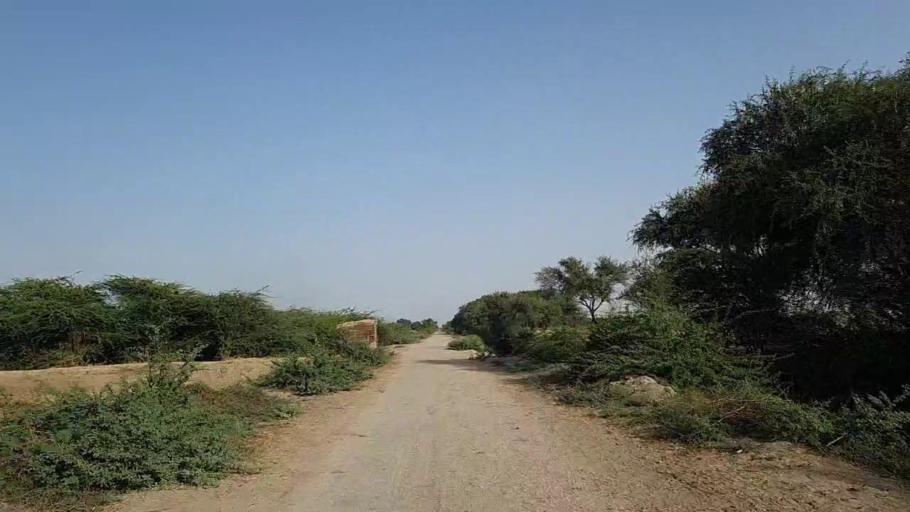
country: PK
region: Sindh
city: Jati
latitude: 24.2651
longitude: 68.1646
